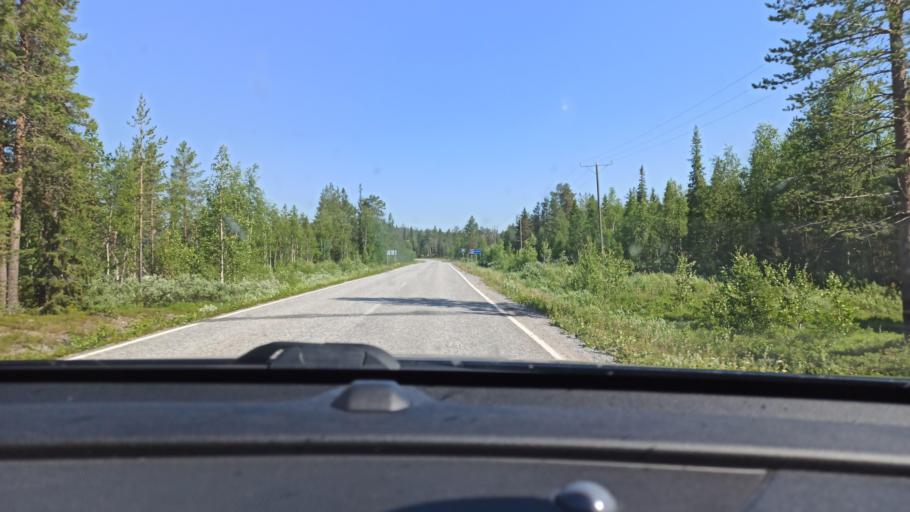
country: FI
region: Lapland
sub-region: Tunturi-Lappi
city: Kolari
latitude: 67.6307
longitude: 24.1571
